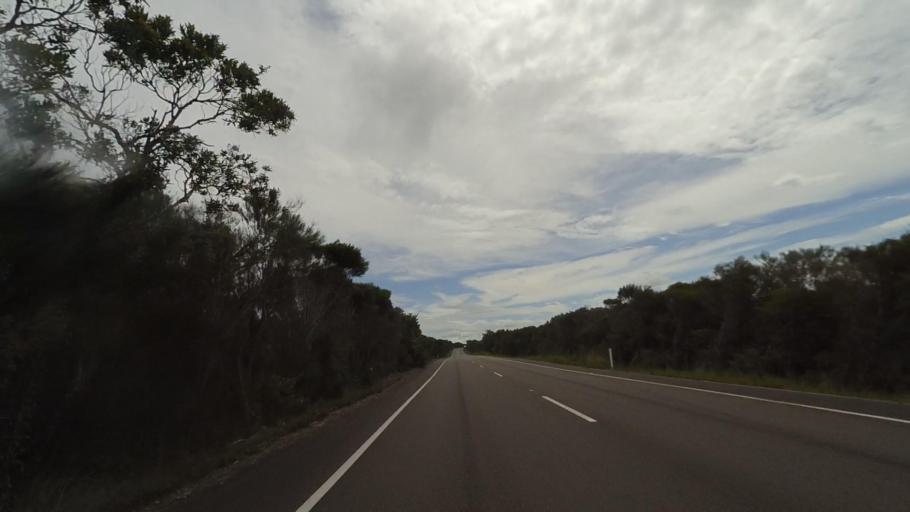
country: AU
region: New South Wales
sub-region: Sutherland Shire
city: Dolans Bay
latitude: -34.1028
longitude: 151.1171
